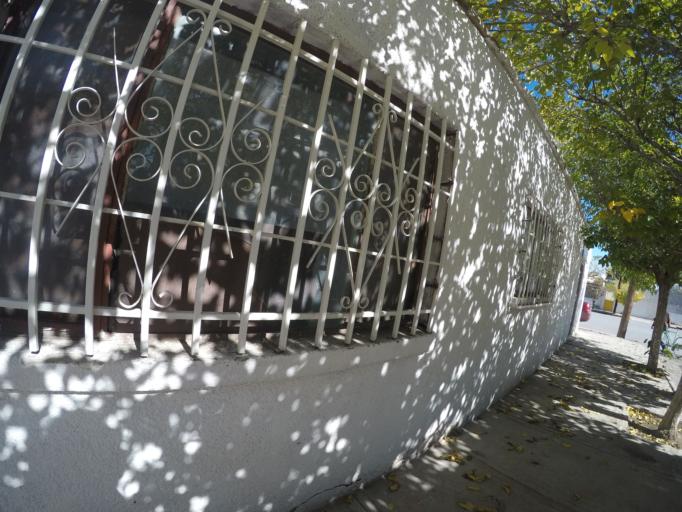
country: MX
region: Chihuahua
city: Ciudad Juarez
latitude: 31.7294
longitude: -106.4280
